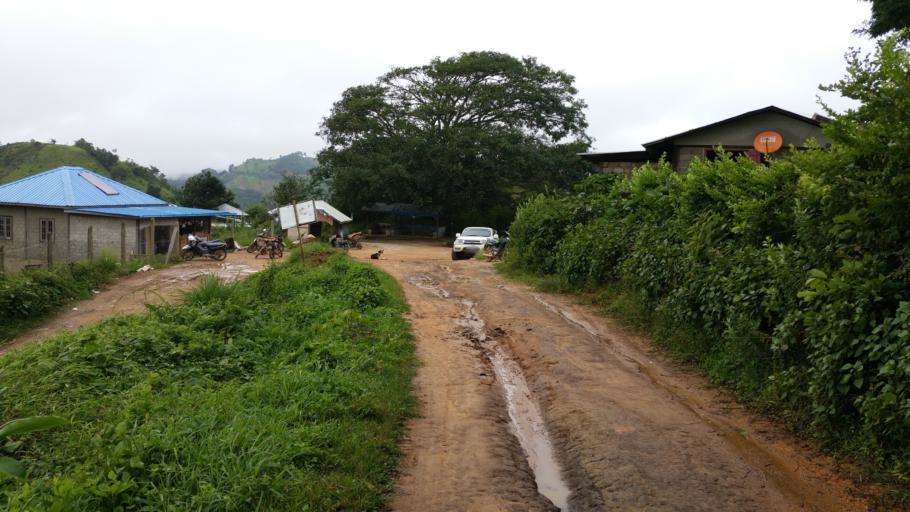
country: MM
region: Mandalay
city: Yamethin
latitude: 20.6100
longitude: 96.5132
